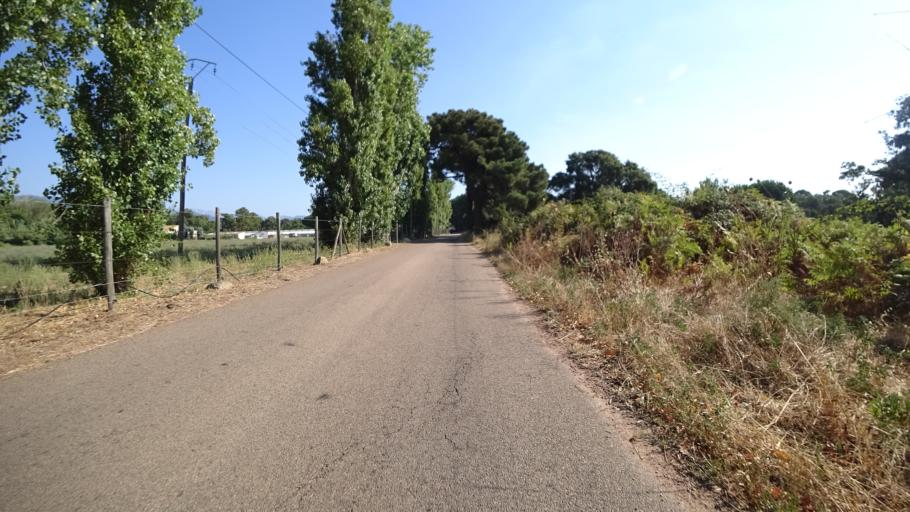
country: FR
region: Corsica
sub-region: Departement de la Corse-du-Sud
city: Porto-Vecchio
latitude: 41.6299
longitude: 9.3303
